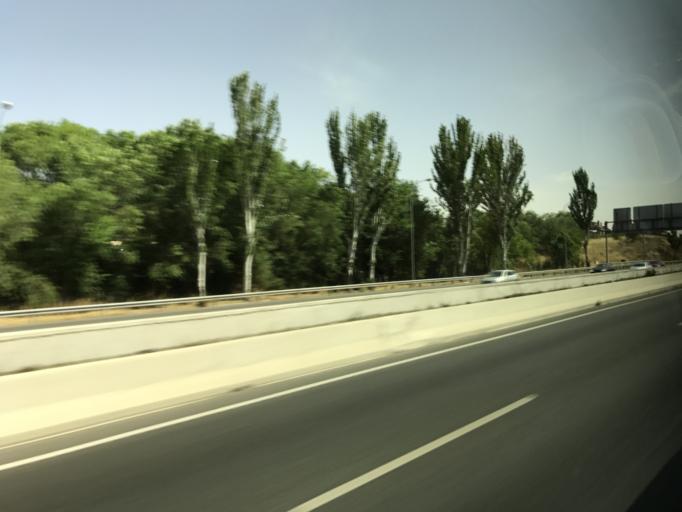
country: ES
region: Madrid
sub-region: Provincia de Madrid
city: Vicalvaro
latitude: 40.4190
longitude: -3.6076
